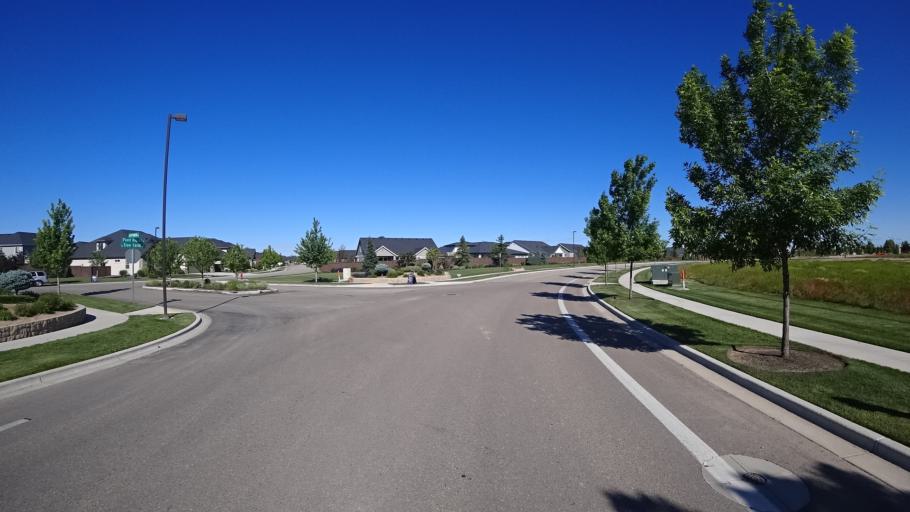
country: US
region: Idaho
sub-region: Ada County
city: Star
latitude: 43.6598
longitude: -116.4429
